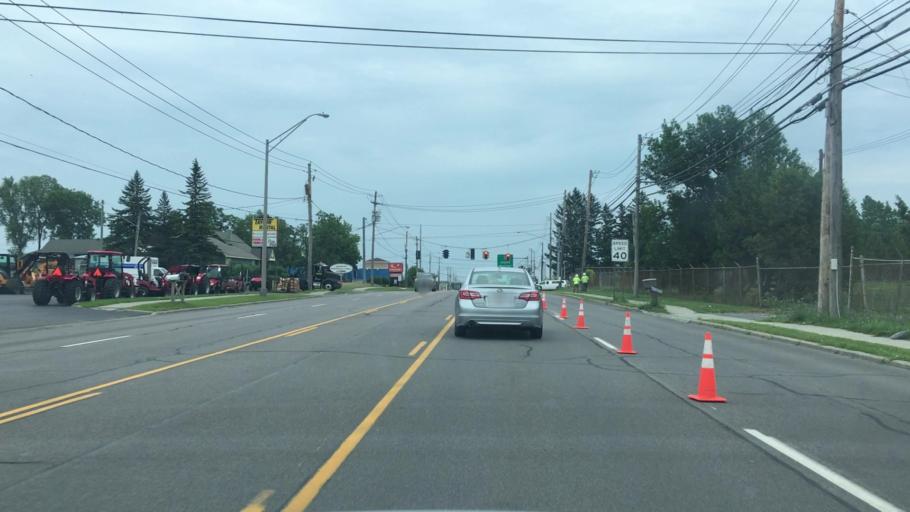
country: US
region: New York
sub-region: Clinton County
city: Plattsburgh West
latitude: 44.6959
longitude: -73.5021
